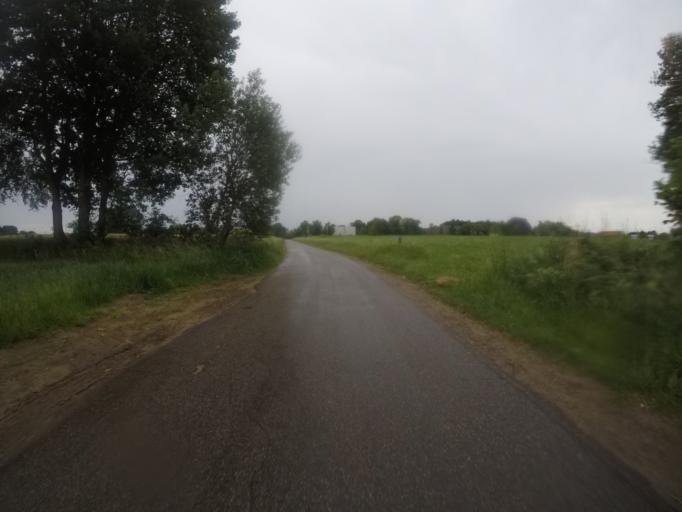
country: DE
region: North Rhine-Westphalia
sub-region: Regierungsbezirk Munster
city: Isselburg
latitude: 51.8261
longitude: 6.5130
